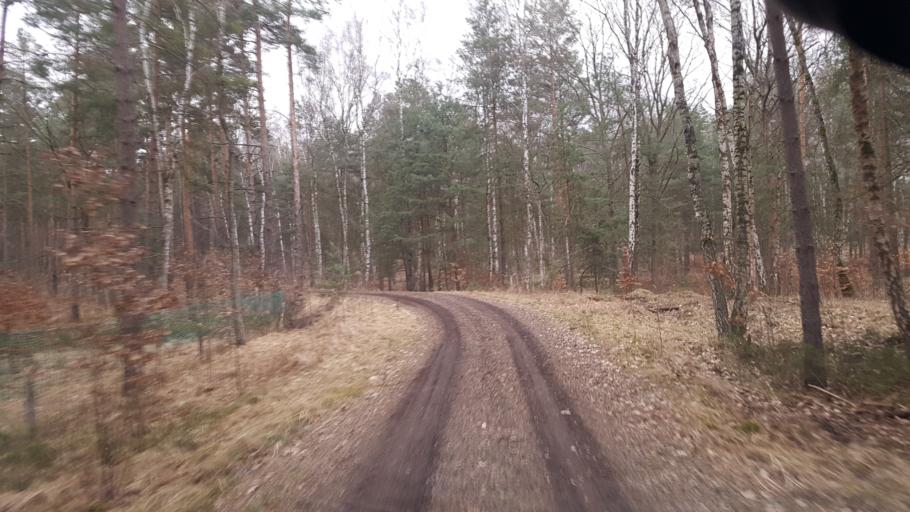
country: DE
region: Brandenburg
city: Schonborn
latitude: 51.6142
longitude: 13.4615
